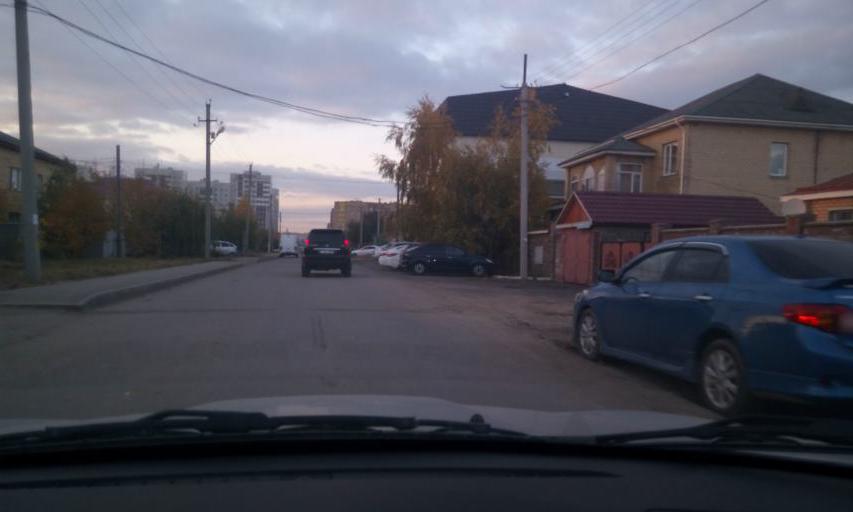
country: KZ
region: Astana Qalasy
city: Astana
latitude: 51.1370
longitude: 71.4881
